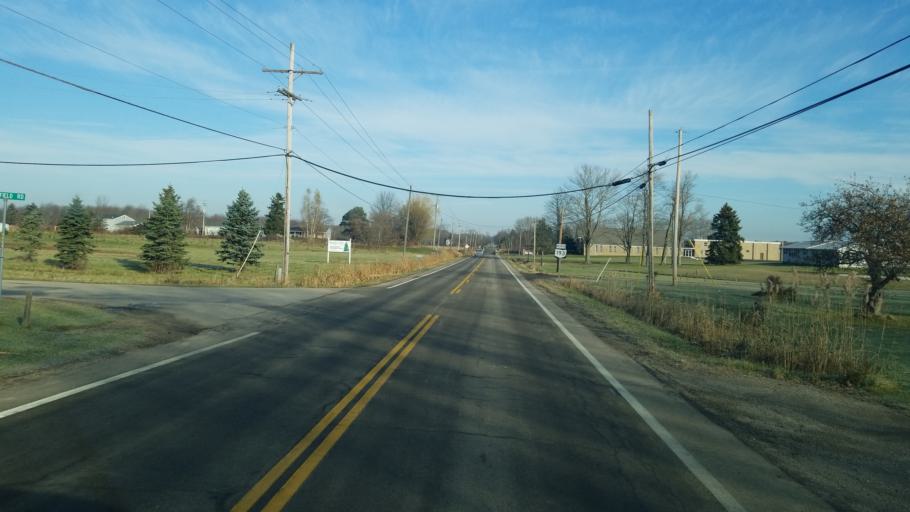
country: US
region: Ohio
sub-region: Ashtabula County
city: North Kingsville
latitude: 41.8238
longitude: -80.6641
